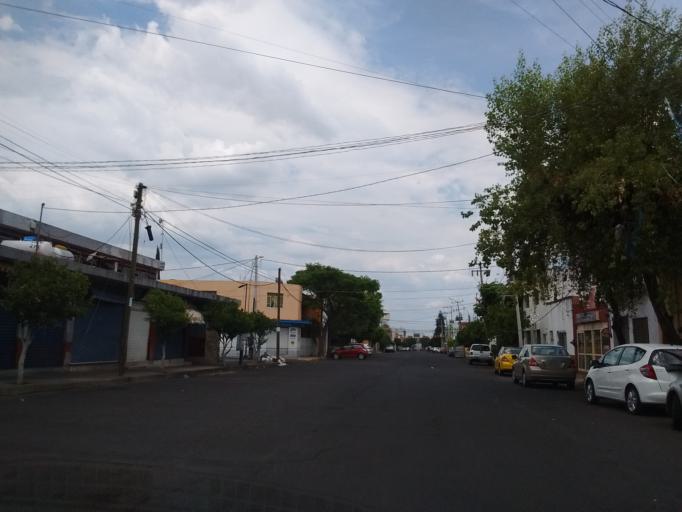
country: MX
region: Jalisco
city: Guadalajara
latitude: 20.6677
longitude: -103.3645
